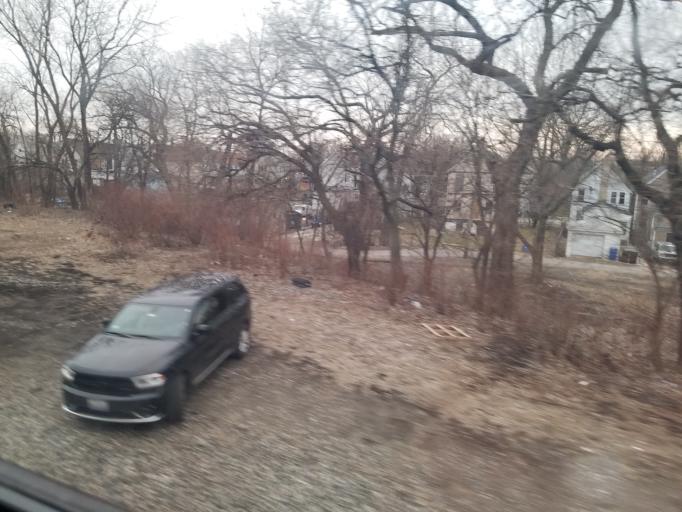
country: US
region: Illinois
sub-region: Cook County
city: Chicago
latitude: 41.7918
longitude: -87.6352
